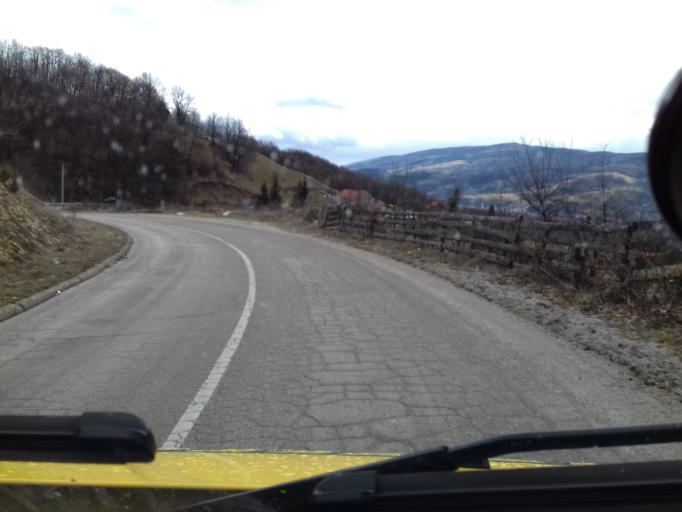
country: BA
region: Federation of Bosnia and Herzegovina
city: Turbe
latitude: 44.2615
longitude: 17.5454
